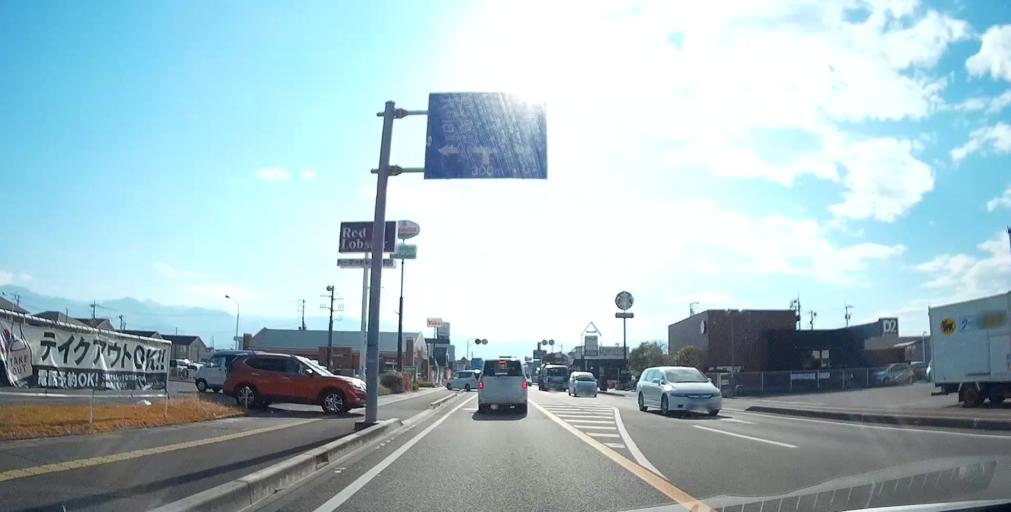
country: JP
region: Yamanashi
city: Isawa
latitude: 35.6489
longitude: 138.6129
